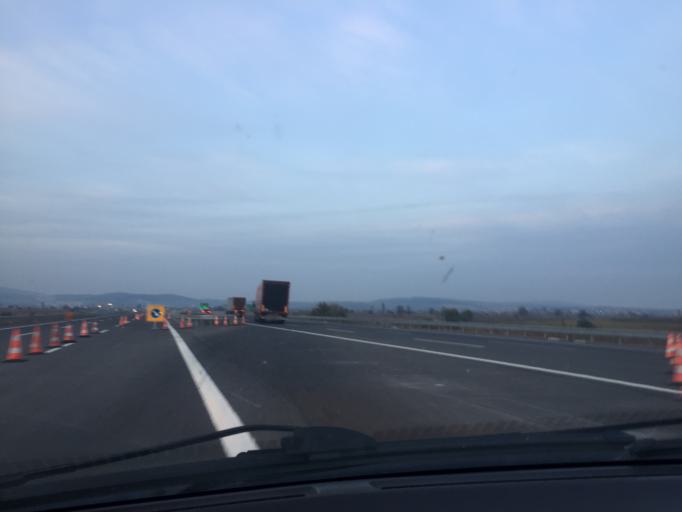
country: TR
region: Manisa
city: Halitpasa
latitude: 38.7433
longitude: 27.6587
